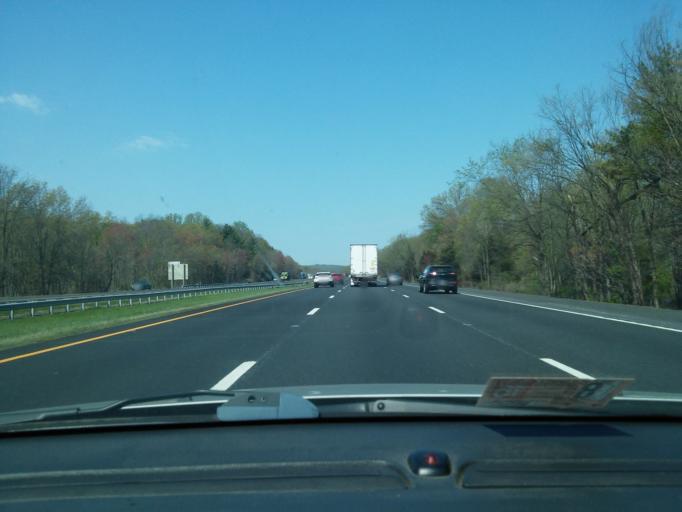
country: US
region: New Jersey
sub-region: Somerset County
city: Warren Township
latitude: 40.6472
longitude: -74.5321
